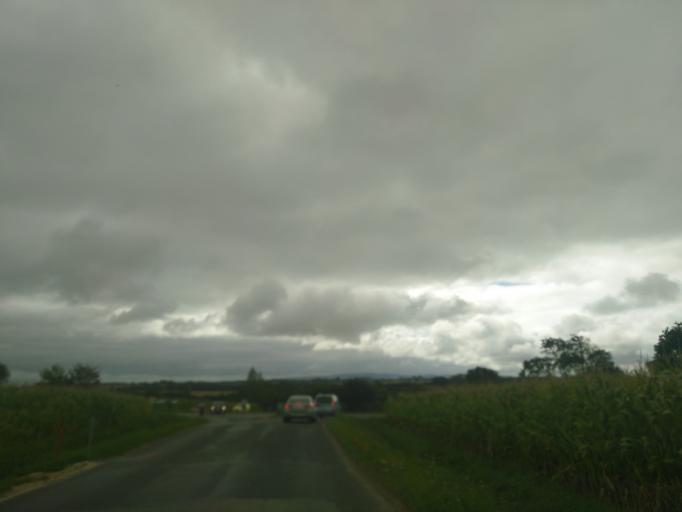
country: FR
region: Brittany
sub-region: Departement du Finistere
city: Plomodiern
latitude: 48.1568
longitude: -4.2458
